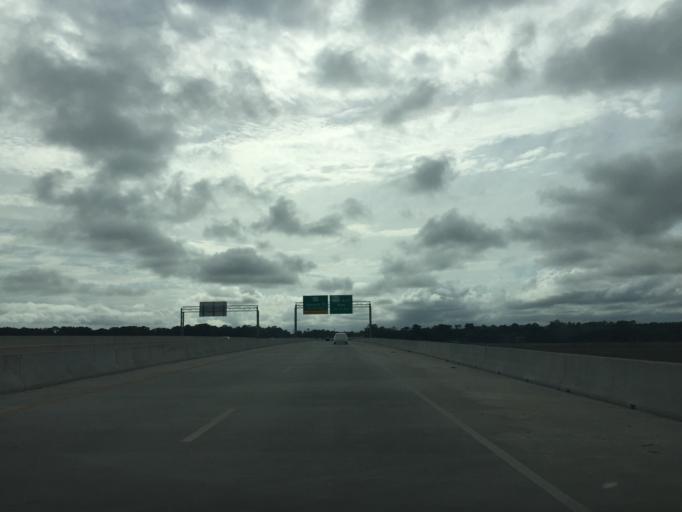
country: US
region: Georgia
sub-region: Chatham County
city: Montgomery
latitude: 31.9751
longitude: -81.1178
